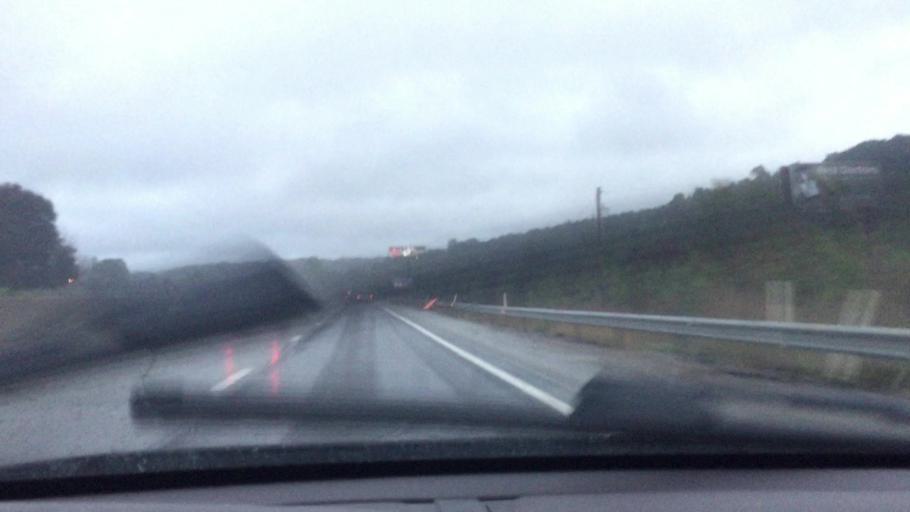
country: US
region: Pennsylvania
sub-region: Washington County
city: Bentleyville
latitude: 40.1471
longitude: -80.0290
